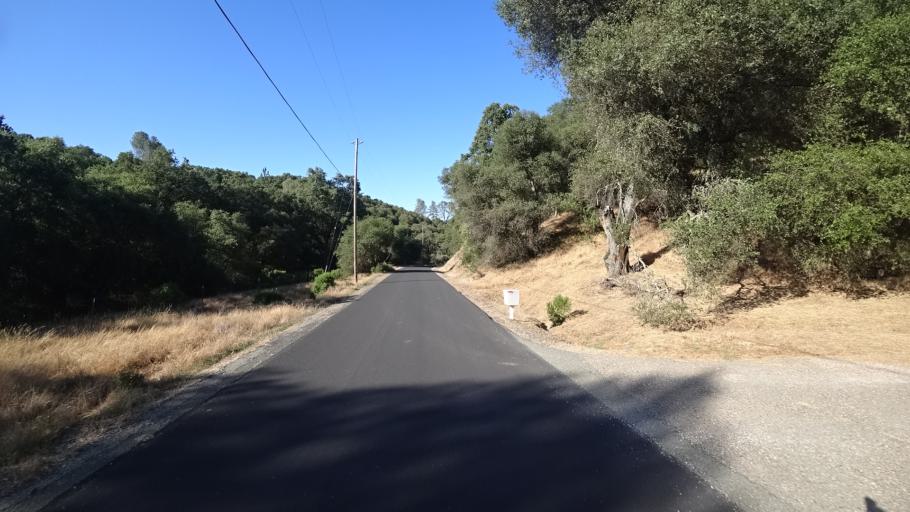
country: US
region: California
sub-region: Calaveras County
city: San Andreas
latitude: 38.2468
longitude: -120.7069
